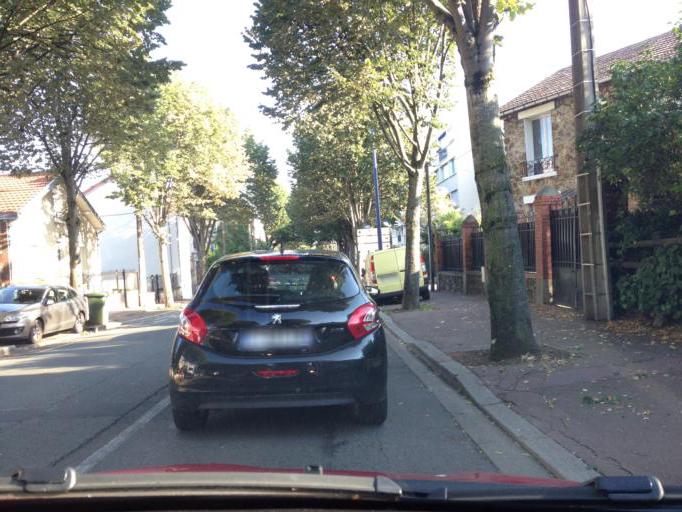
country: FR
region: Ile-de-France
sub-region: Departement des Hauts-de-Seine
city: Clamart
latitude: 48.8101
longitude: 2.2585
